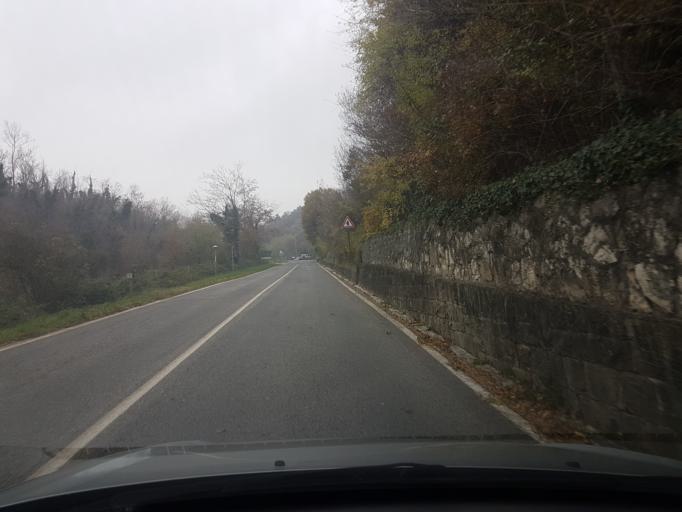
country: IT
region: Friuli Venezia Giulia
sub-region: Provincia di Trieste
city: Domio
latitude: 45.6321
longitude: 13.8414
